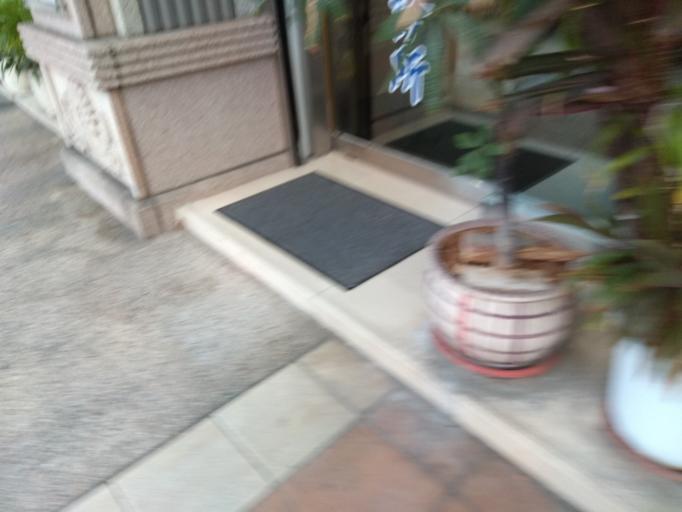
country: TW
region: Taiwan
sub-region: Hsinchu
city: Zhubei
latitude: 24.8212
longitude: 121.0261
